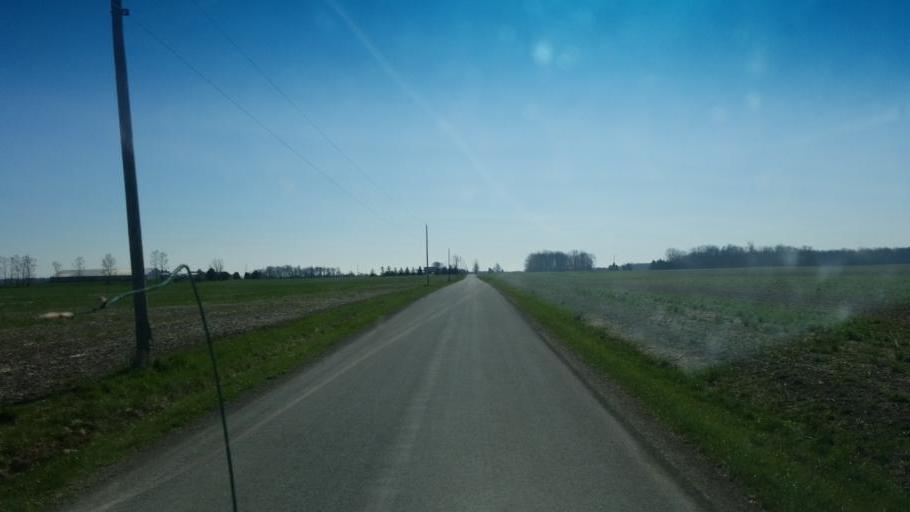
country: US
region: Ohio
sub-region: Hardin County
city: Kenton
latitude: 40.7020
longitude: -83.5354
